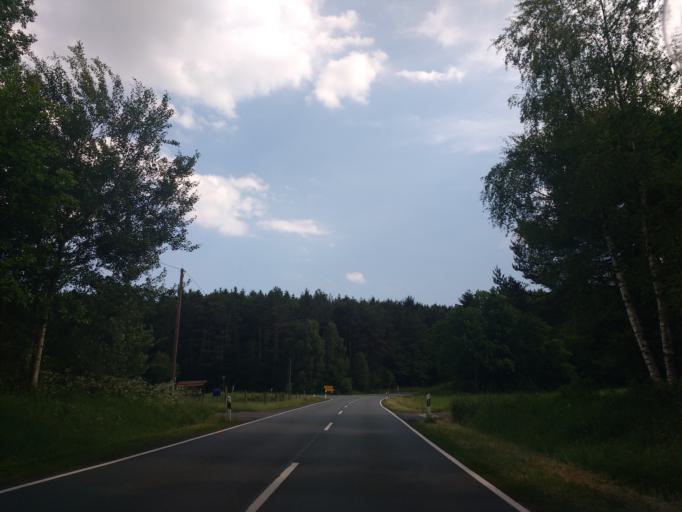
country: DE
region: Hesse
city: Frankenberg
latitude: 51.0246
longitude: 8.8243
